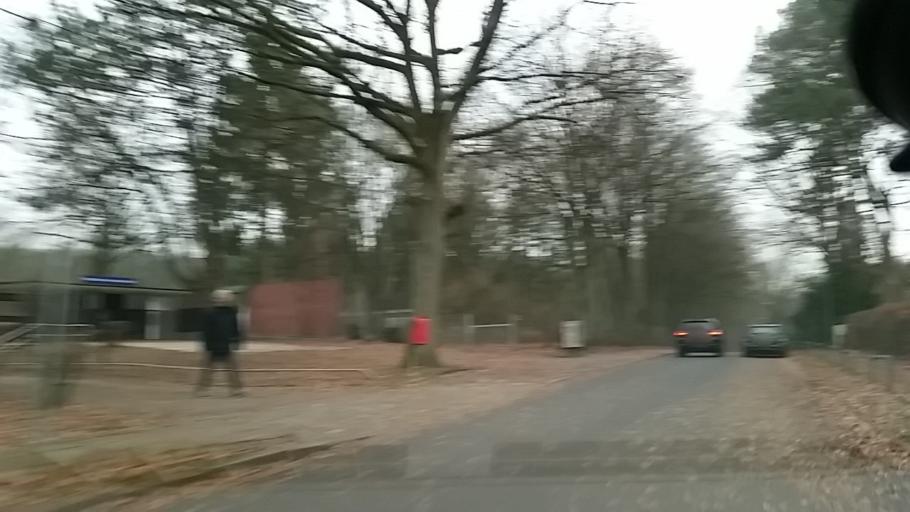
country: DE
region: Schleswig-Holstein
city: Rellingen
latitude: 53.5756
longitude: 9.7960
